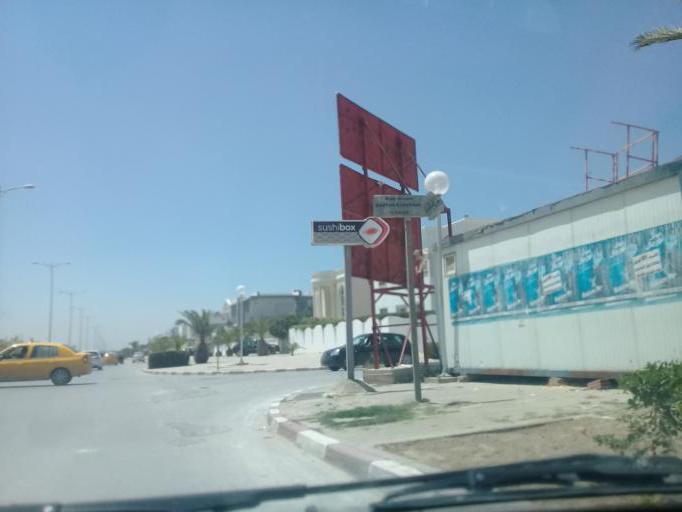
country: TN
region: Tunis
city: La Goulette
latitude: 36.8427
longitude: 10.2760
